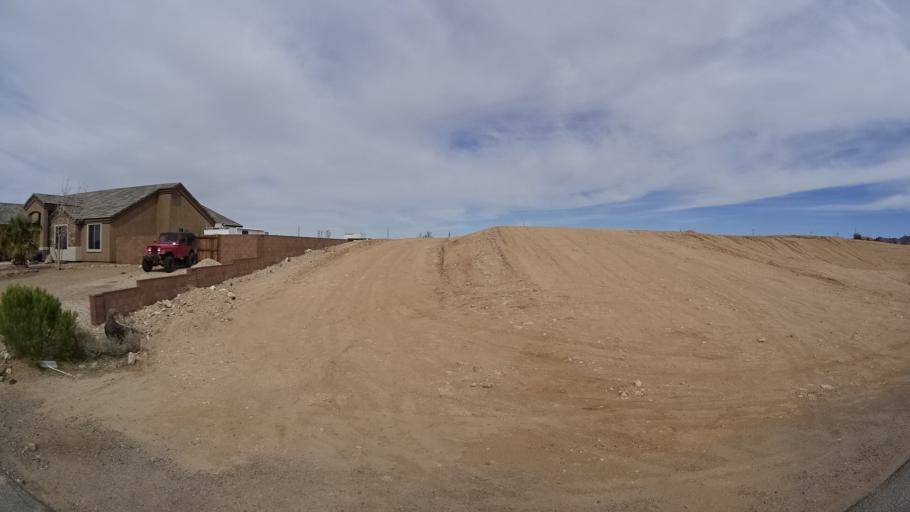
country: US
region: Arizona
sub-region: Mohave County
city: Kingman
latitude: 35.1782
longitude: -113.9977
